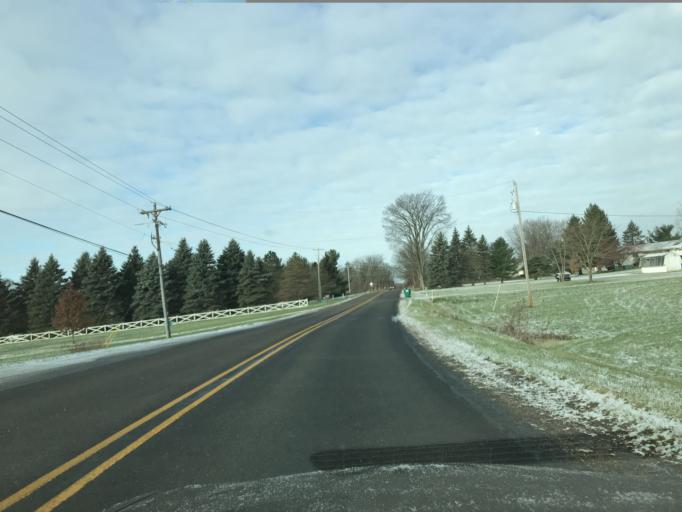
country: US
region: Michigan
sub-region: Eaton County
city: Dimondale
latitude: 42.6402
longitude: -84.6371
